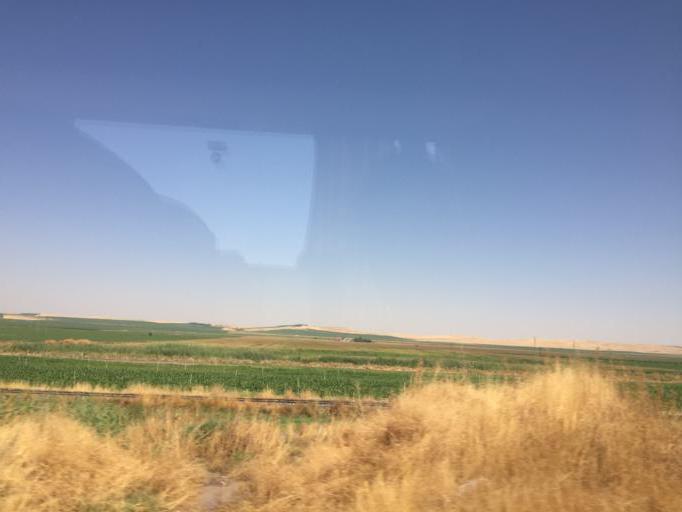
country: TR
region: Diyarbakir
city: Tepe
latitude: 37.8501
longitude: 40.7791
